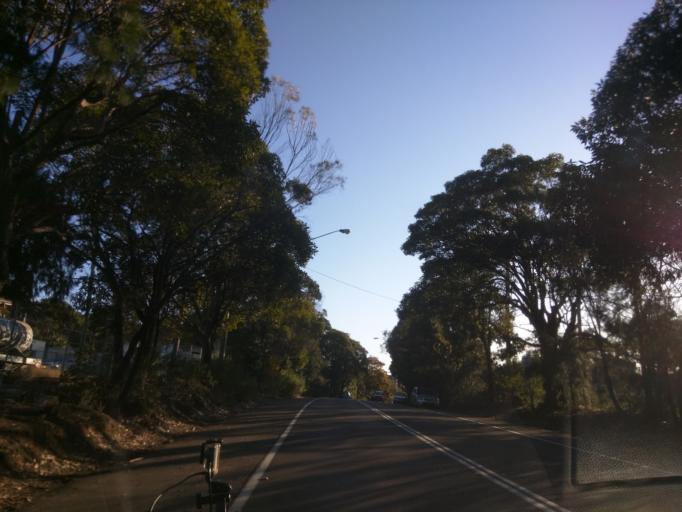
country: AU
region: New South Wales
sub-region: Sutherland Shire
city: Loftus
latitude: -34.0365
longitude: 151.0546
